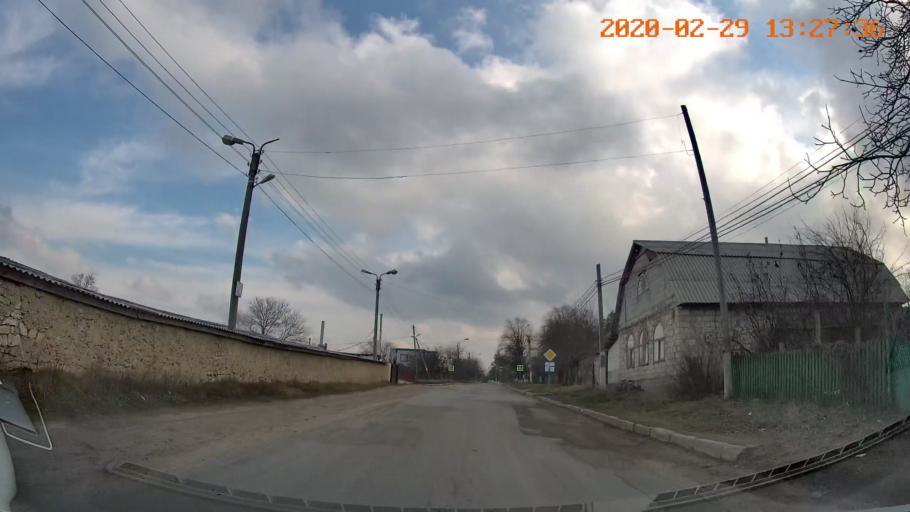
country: MD
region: Telenesti
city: Camenca
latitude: 47.9111
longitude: 28.6432
